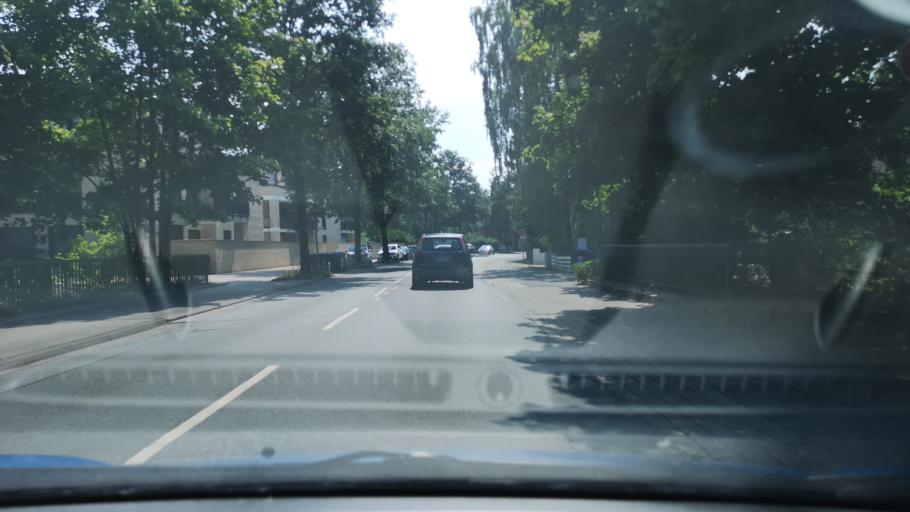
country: DE
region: Lower Saxony
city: Isernhagen Farster Bauerschaft
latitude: 52.4369
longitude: 9.8025
